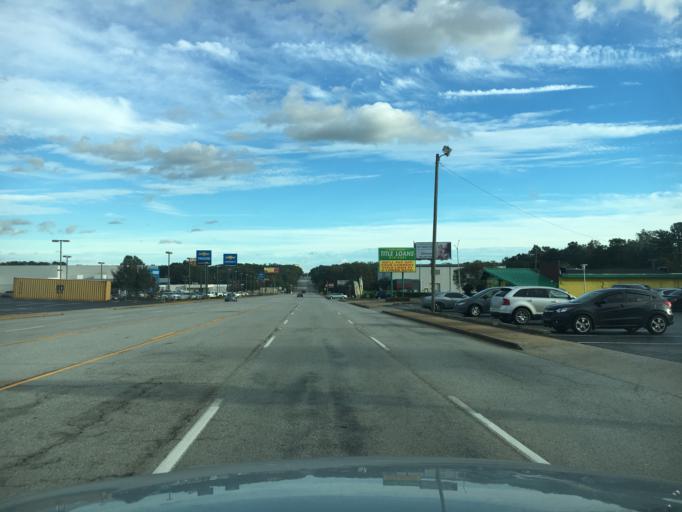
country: US
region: South Carolina
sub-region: Spartanburg County
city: Saxon
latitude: 34.9712
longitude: -81.9541
